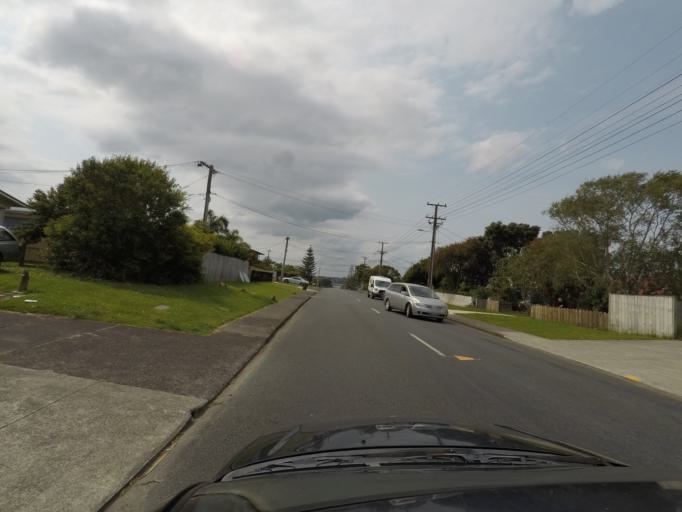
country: NZ
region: Auckland
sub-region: Auckland
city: Rosebank
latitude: -36.8278
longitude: 174.6465
